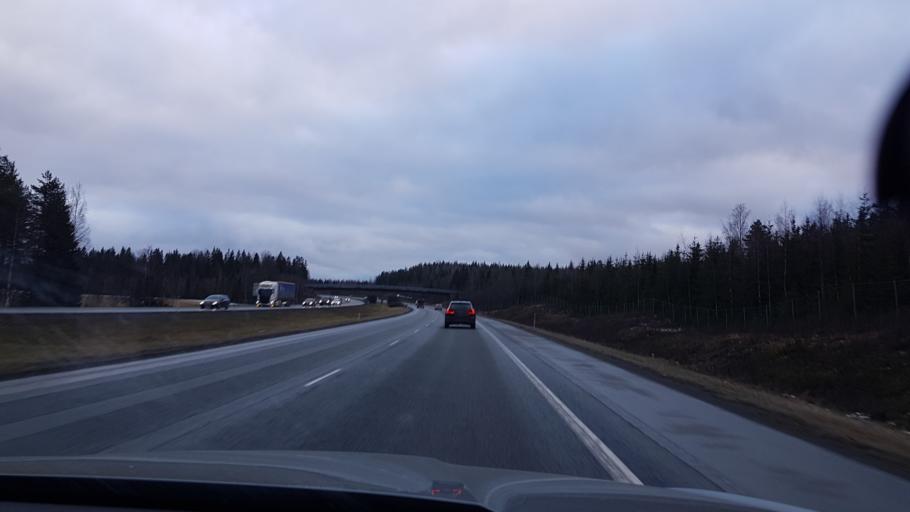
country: FI
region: Pirkanmaa
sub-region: Tampere
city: Lempaeaelae
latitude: 61.2836
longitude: 23.8091
